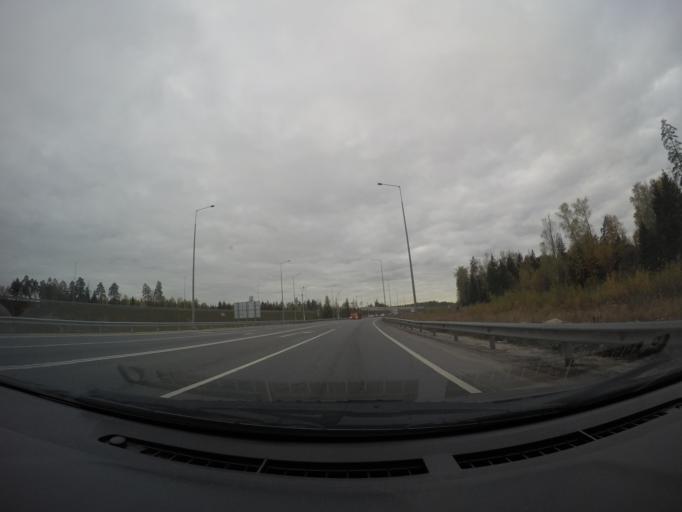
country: RU
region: Moskovskaya
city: Fryazevo
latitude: 55.6975
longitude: 38.4341
